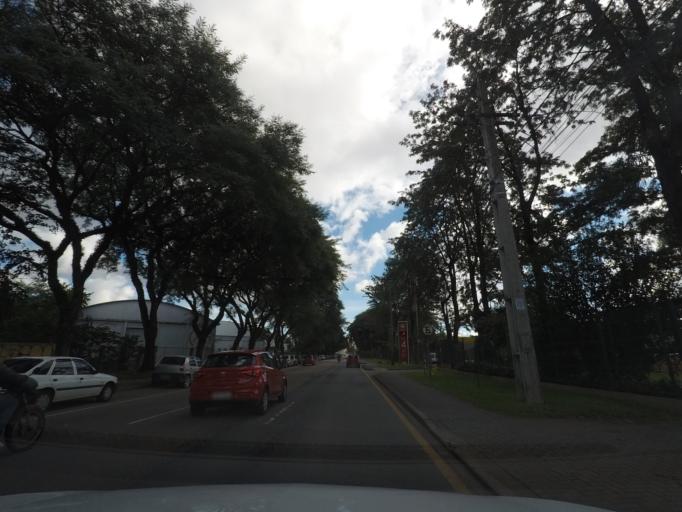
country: BR
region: Parana
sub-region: Curitiba
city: Curitiba
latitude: -25.4561
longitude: -49.2509
